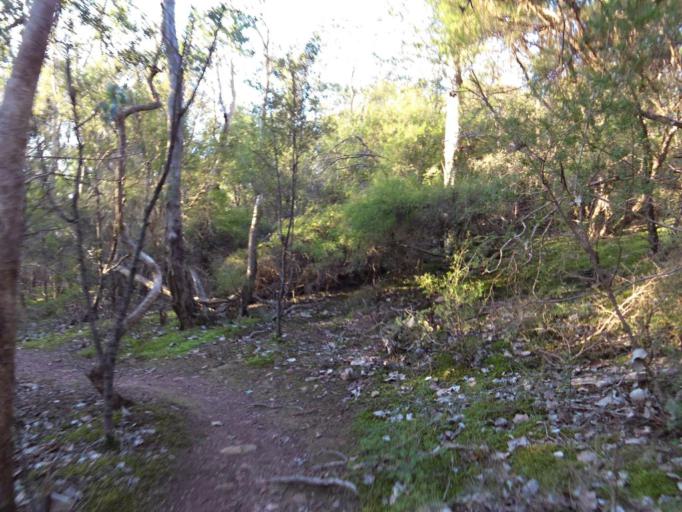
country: AU
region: Victoria
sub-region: Nillumbik
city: North Warrandyte
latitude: -37.7228
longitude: 145.2366
